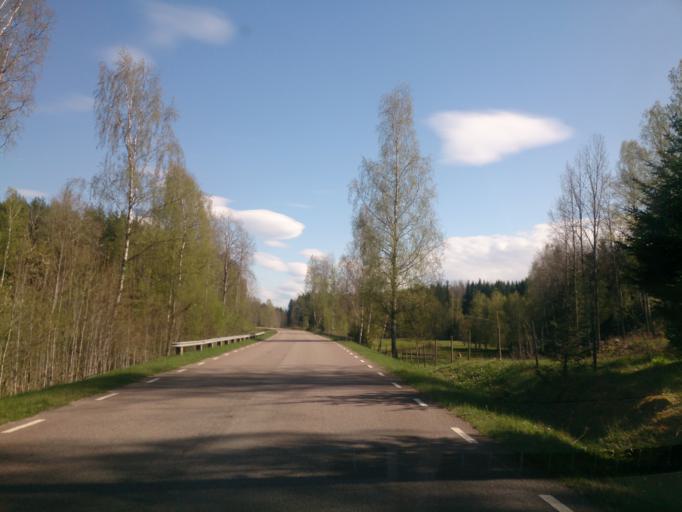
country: SE
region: OEstergoetland
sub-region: Linkopings Kommun
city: Ljungsbro
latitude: 58.6070
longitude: 15.4801
